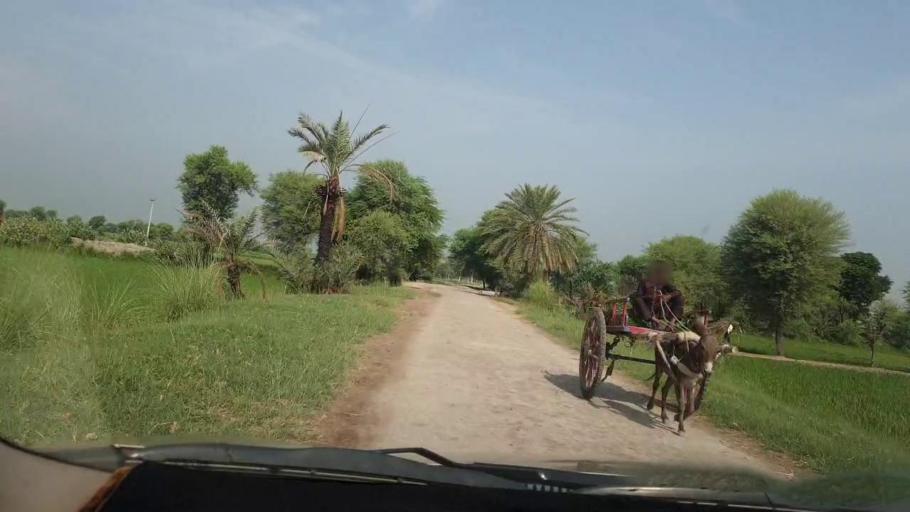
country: PK
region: Sindh
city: Goth Garelo
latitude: 27.4487
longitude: 68.0274
